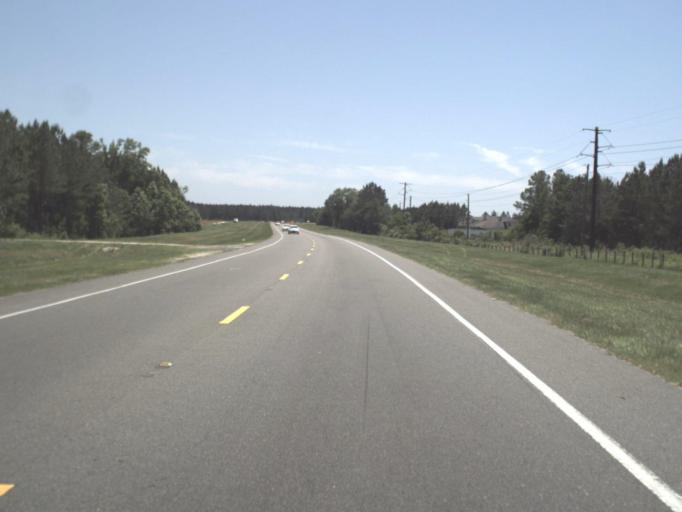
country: US
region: Florida
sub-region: Clay County
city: Lakeside
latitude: 30.1838
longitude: -81.8363
